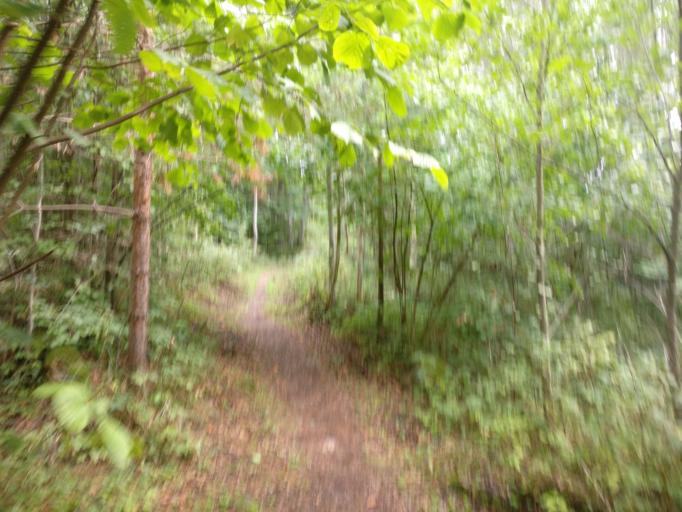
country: LV
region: Engure
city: Smarde
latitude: 56.9917
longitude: 23.4335
